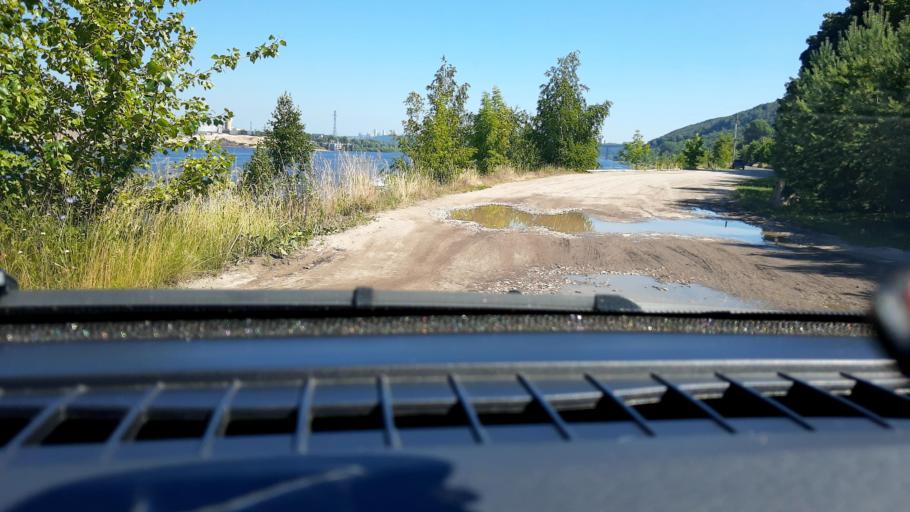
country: RU
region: Nizjnij Novgorod
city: Nizhniy Novgorod
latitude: 56.2289
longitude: 43.9193
